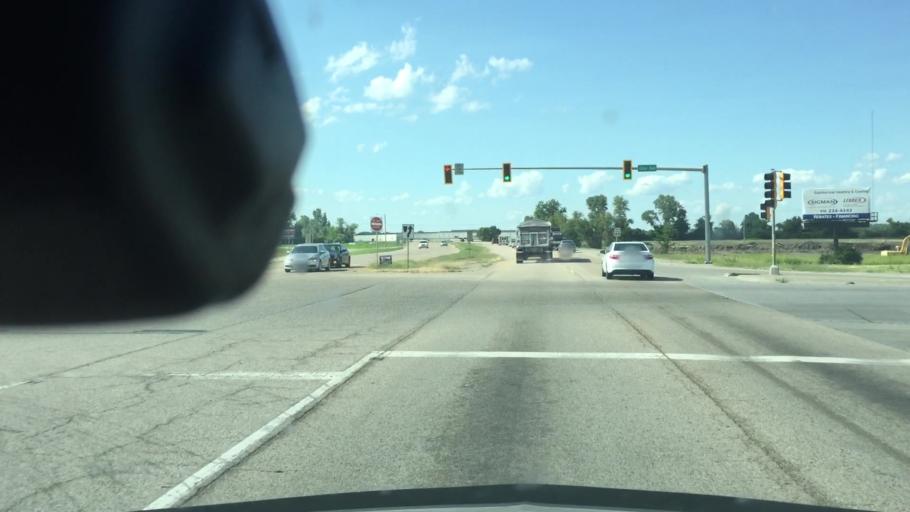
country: US
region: Illinois
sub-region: Saint Clair County
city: East Saint Louis
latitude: 38.6525
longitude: -90.1330
